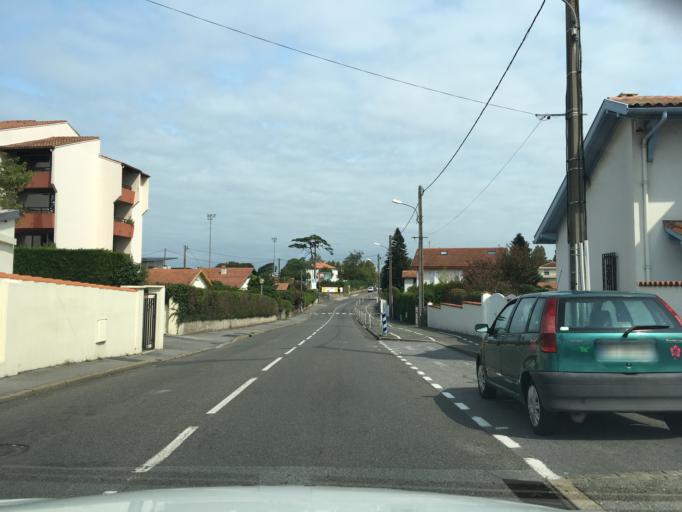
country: FR
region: Aquitaine
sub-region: Departement des Pyrenees-Atlantiques
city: Anglet
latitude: 43.4862
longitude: -1.5141
